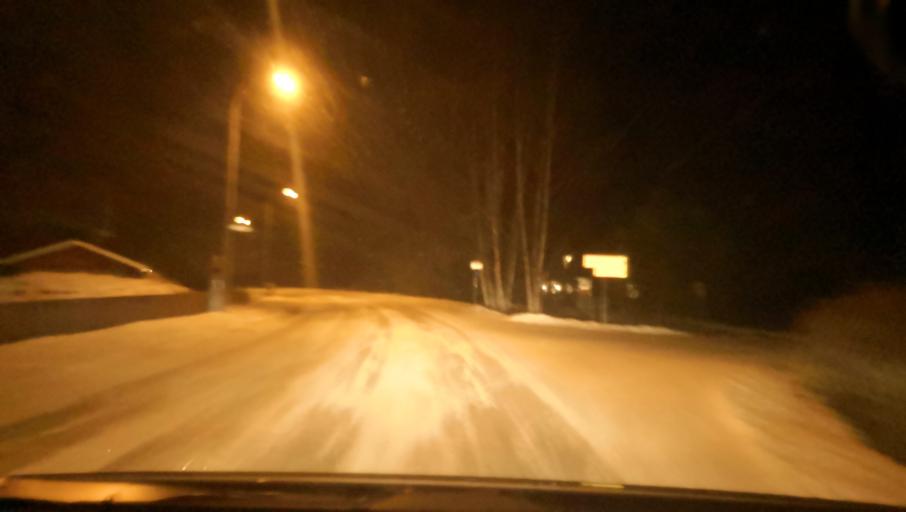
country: SE
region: Uppsala
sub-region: Heby Kommun
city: Tarnsjo
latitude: 60.1443
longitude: 16.9117
